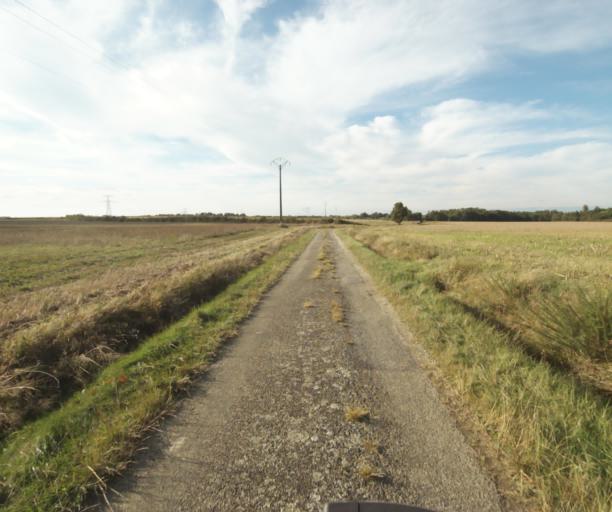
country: FR
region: Midi-Pyrenees
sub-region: Departement du Tarn-et-Garonne
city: Finhan
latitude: 43.9076
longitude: 1.1122
